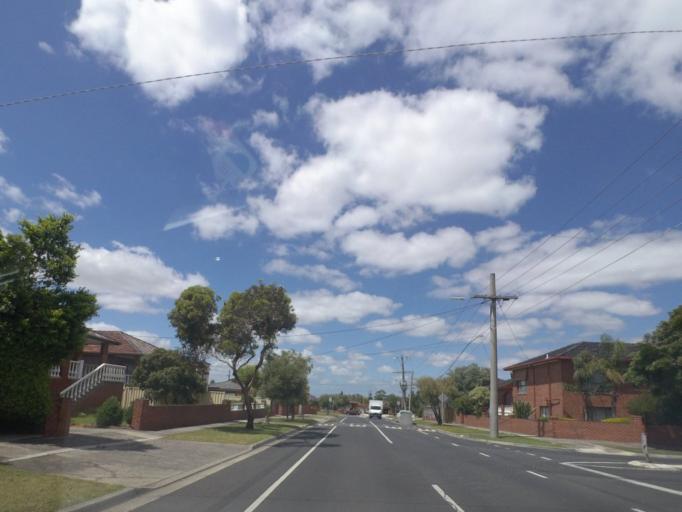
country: AU
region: Victoria
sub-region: Whittlesea
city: Lalor
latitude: -37.6704
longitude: 144.9948
